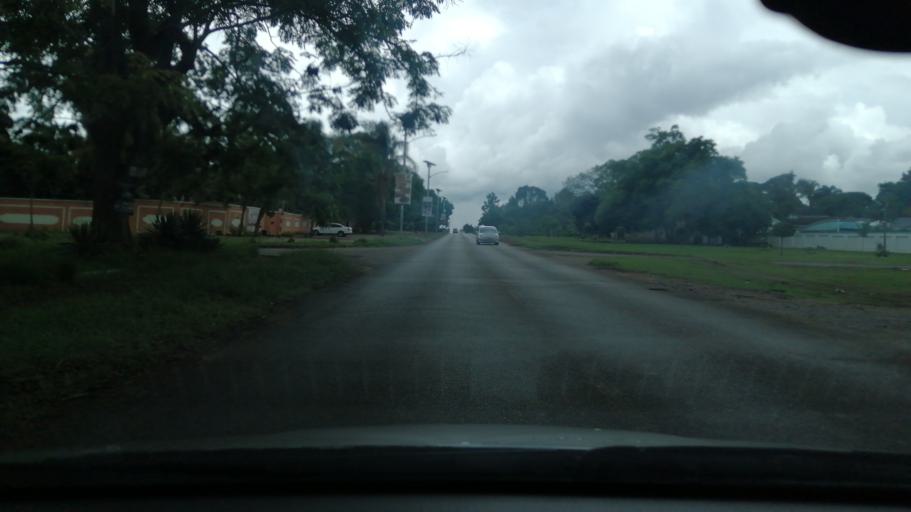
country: ZW
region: Harare
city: Harare
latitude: -17.7950
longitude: 31.0689
